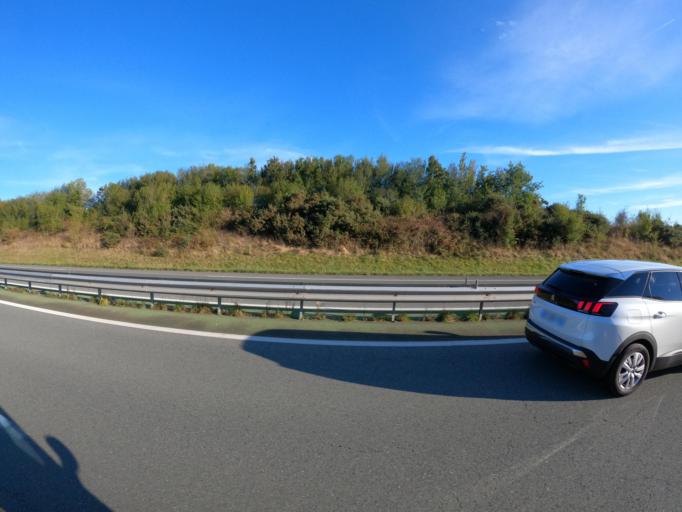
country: FR
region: Pays de la Loire
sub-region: Departement de Maine-et-Loire
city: Trementines
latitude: 47.1763
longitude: -0.7890
